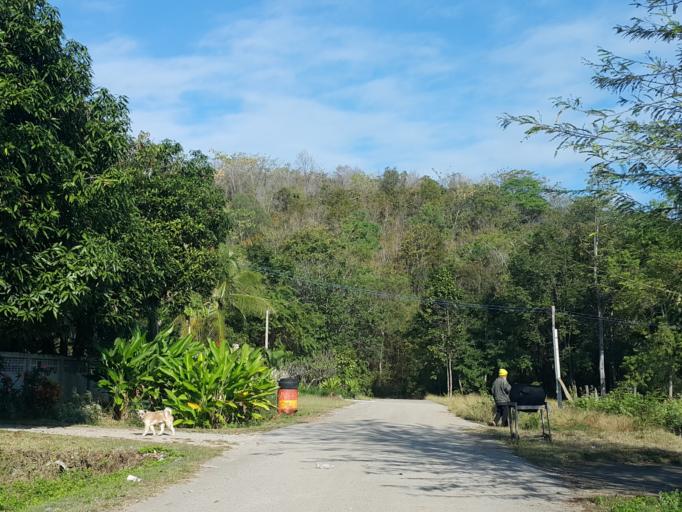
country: TH
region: Lampang
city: Mae Mo
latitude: 18.2832
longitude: 99.6411
